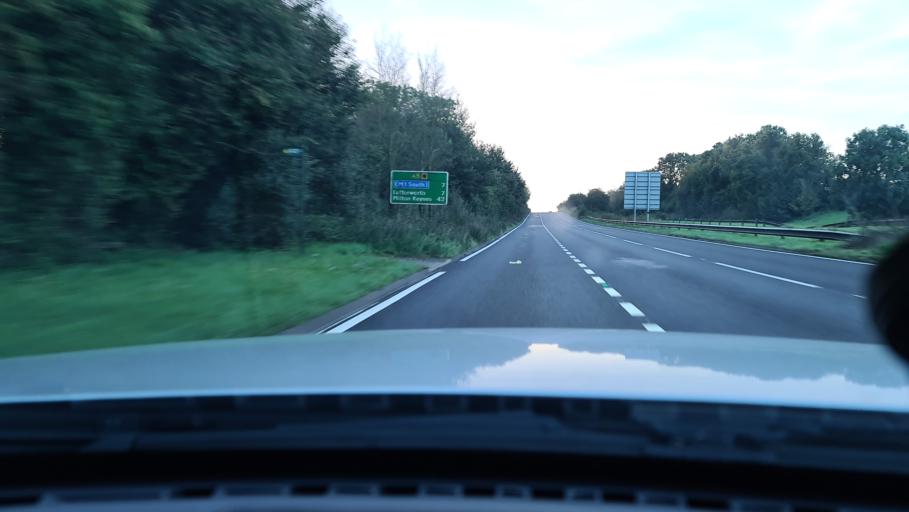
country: GB
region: England
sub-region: Leicestershire
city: Sapcote
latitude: 52.5010
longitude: -1.3229
